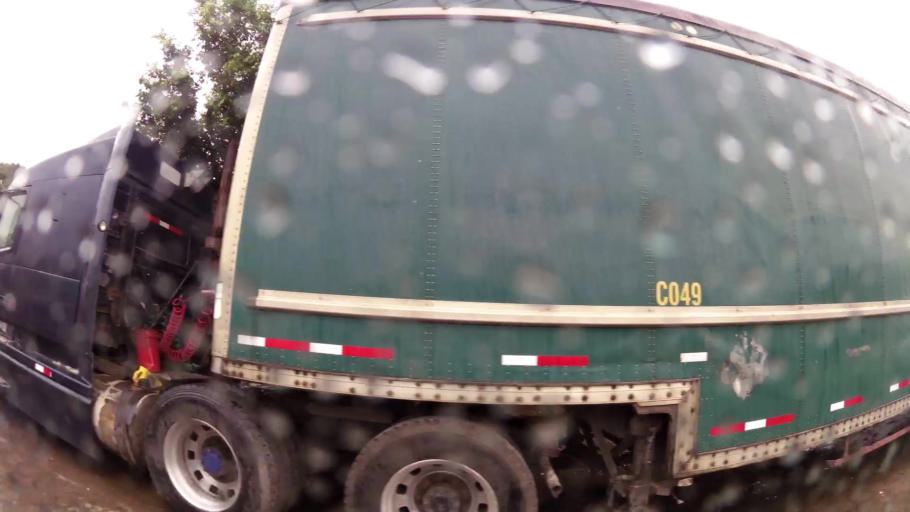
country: BO
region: Santa Cruz
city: Santa Cruz de la Sierra
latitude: -17.7704
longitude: -63.1429
